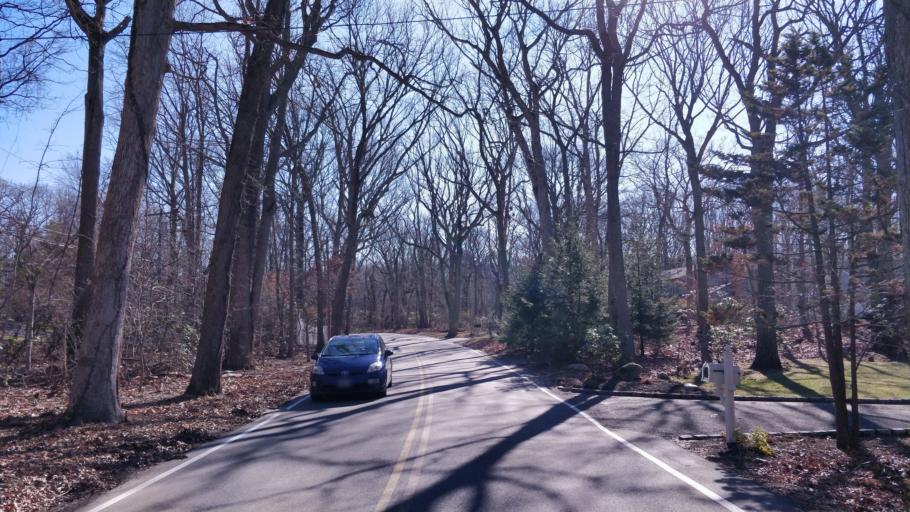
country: US
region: New York
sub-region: Suffolk County
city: Port Jefferson
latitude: 40.9672
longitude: -73.0721
